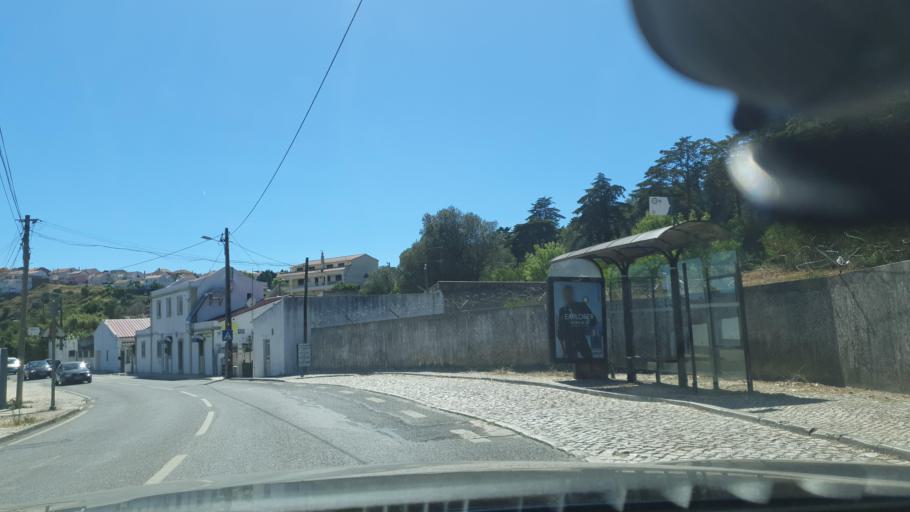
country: PT
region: Lisbon
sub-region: Sintra
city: Belas
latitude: 38.7823
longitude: -9.2468
